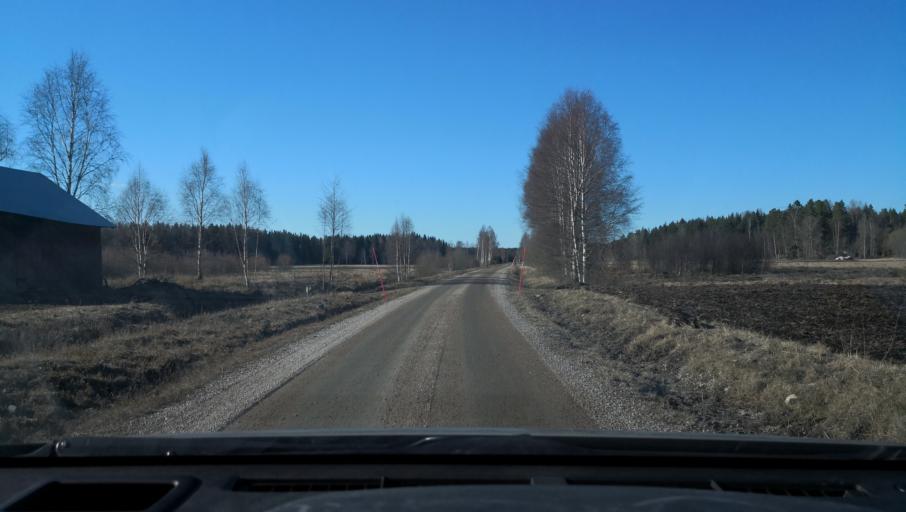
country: SE
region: Vaestmanland
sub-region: Sala Kommun
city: Sala
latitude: 60.1237
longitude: 16.6571
